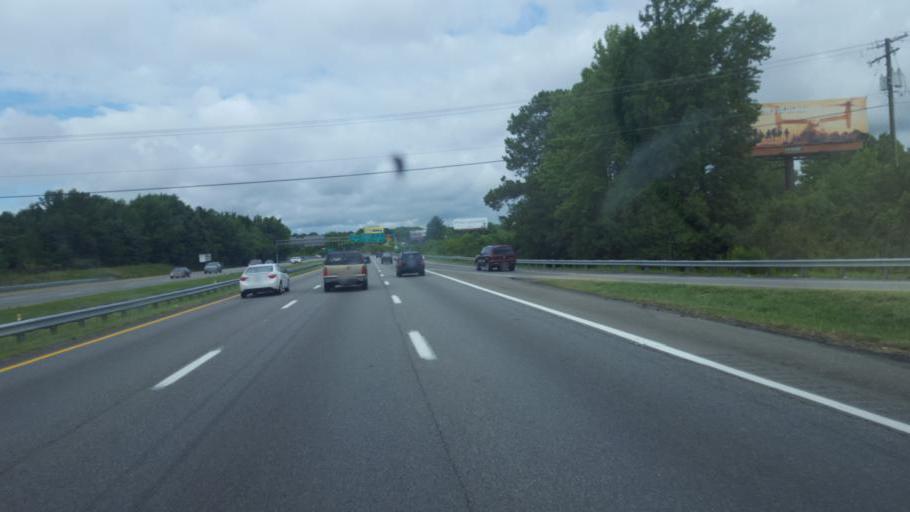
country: US
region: Virginia
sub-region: Henrico County
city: East Highland Park
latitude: 37.5570
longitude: -77.4118
